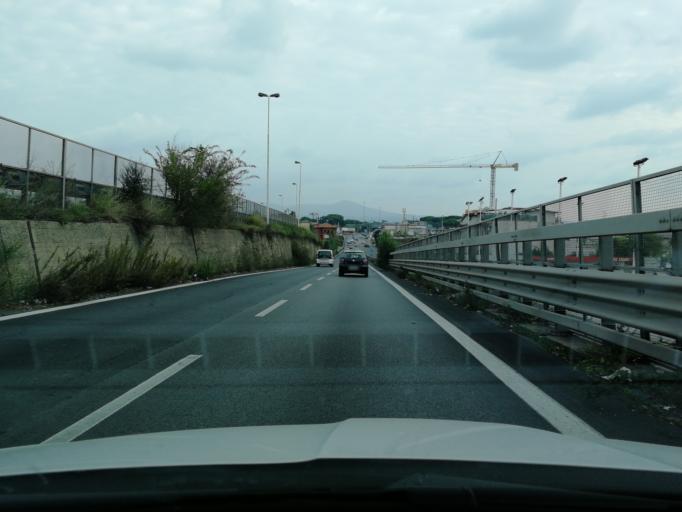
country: IT
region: Latium
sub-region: Citta metropolitana di Roma Capitale
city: Ciampino
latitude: 41.8414
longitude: 12.5860
